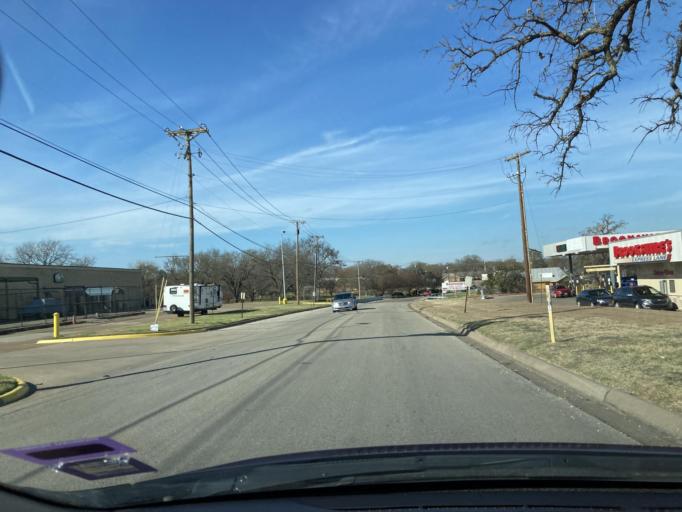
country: US
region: Texas
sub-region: Navarro County
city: Corsicana
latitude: 32.0988
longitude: -96.4716
